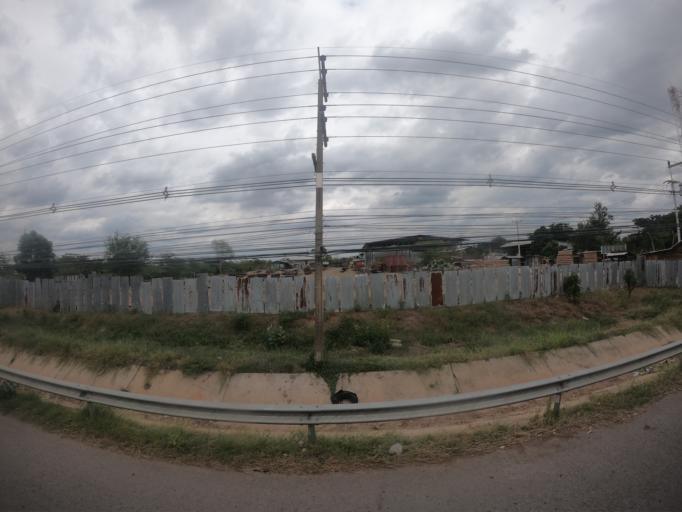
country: TH
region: Nakhon Ratchasima
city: Chok Chai
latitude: 14.7553
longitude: 102.1638
